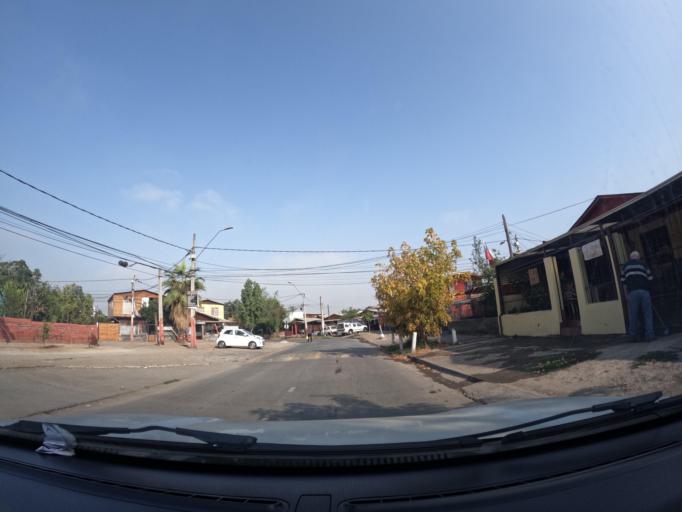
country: CL
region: Santiago Metropolitan
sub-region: Provincia de Santiago
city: Villa Presidente Frei, Nunoa, Santiago, Chile
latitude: -33.4731
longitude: -70.5655
